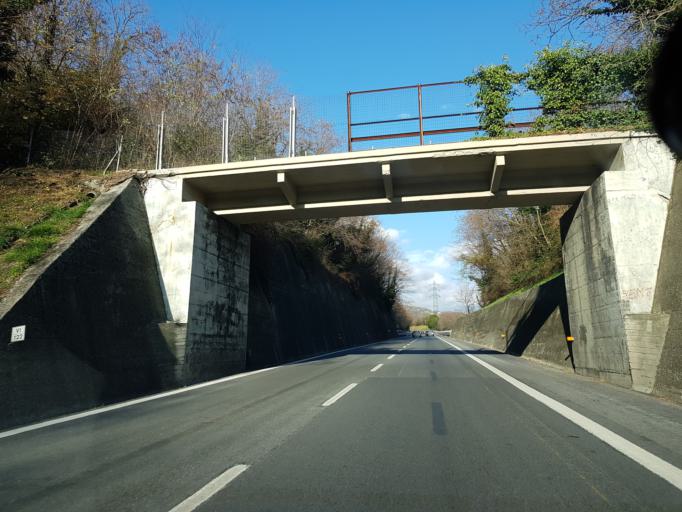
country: IT
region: Liguria
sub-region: Provincia di Genova
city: Manesseno
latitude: 44.4893
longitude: 8.9166
